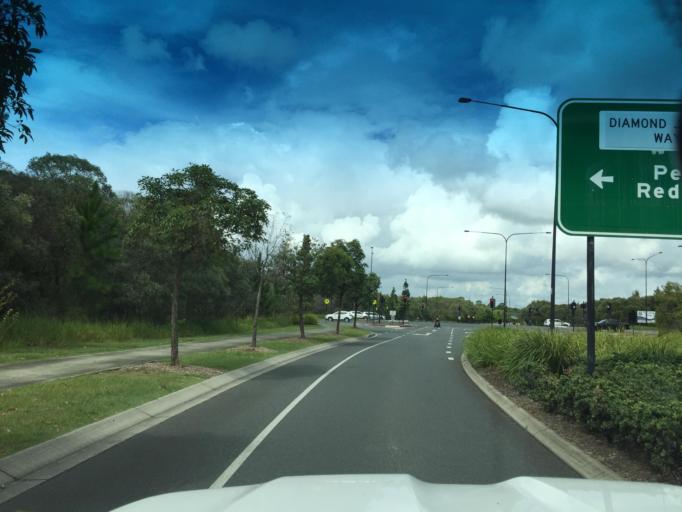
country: AU
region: Queensland
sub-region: Moreton Bay
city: Mango Hill
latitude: -27.2308
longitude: 153.0287
